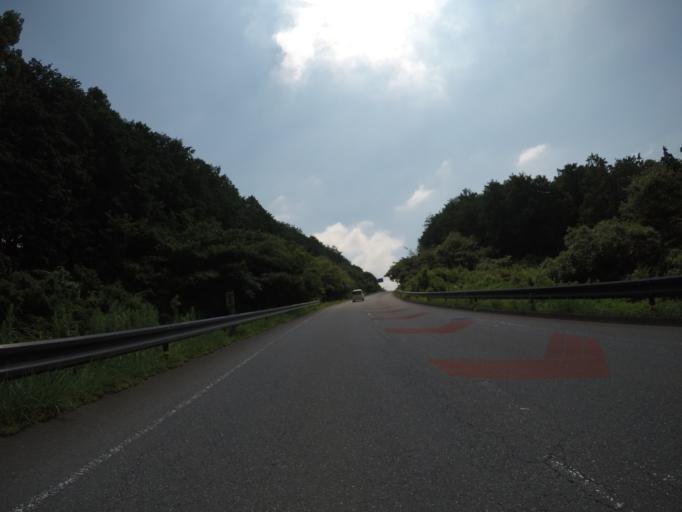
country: JP
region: Shizuoka
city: Fujinomiya
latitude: 35.2632
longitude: 138.6587
